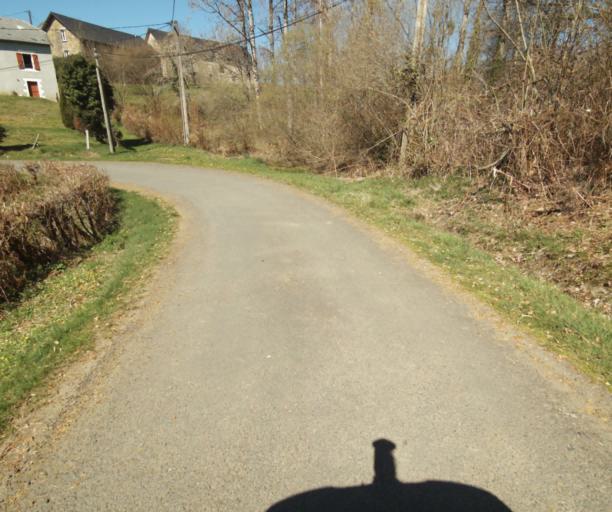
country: FR
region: Limousin
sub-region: Departement de la Correze
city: Saint-Clement
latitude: 45.3268
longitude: 1.7059
